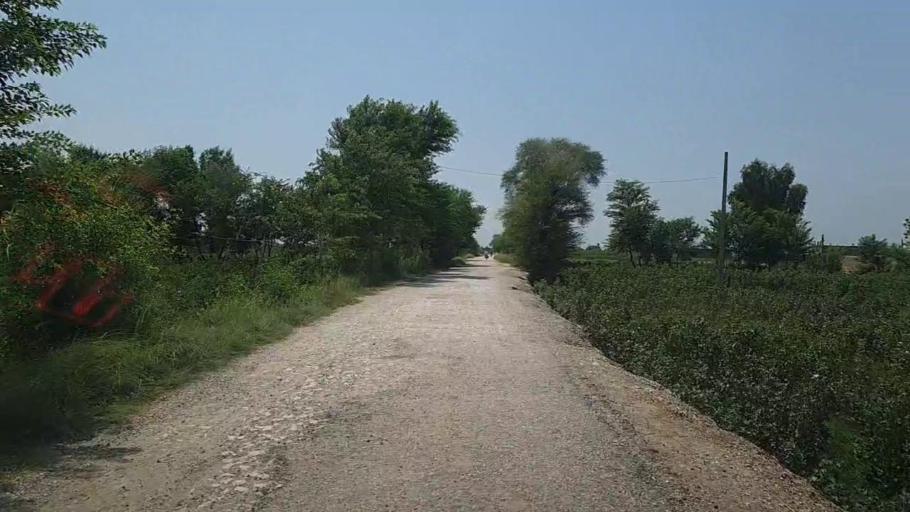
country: PK
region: Sindh
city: Ubauro
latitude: 28.1692
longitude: 69.7636
